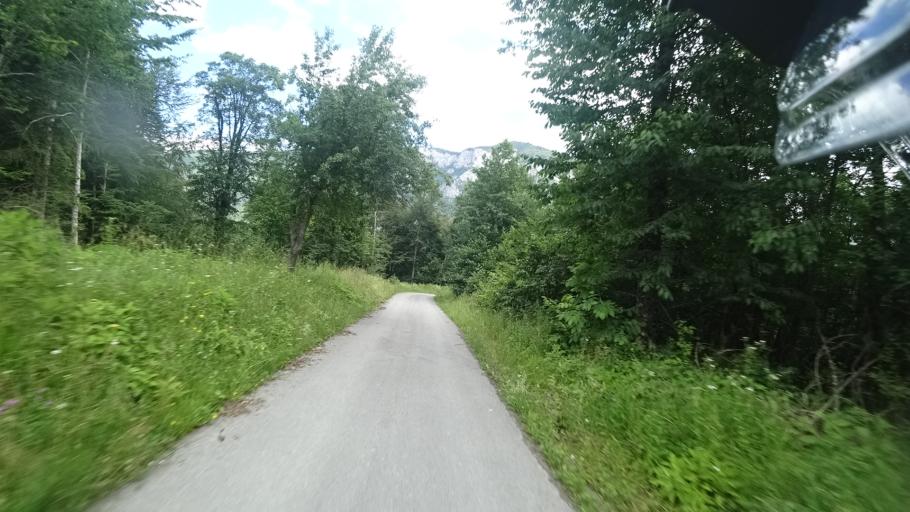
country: SI
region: Osilnica
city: Osilnica
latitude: 45.5244
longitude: 14.7267
